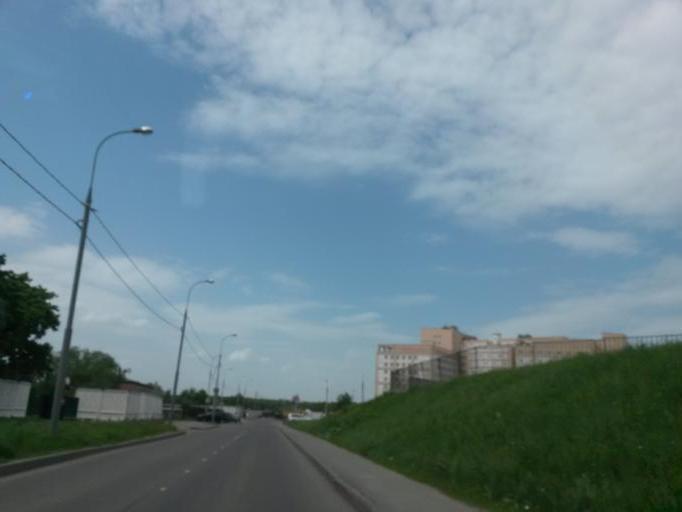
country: RU
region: Moscow
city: Chertanovo Yuzhnoye
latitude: 55.5796
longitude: 37.5850
